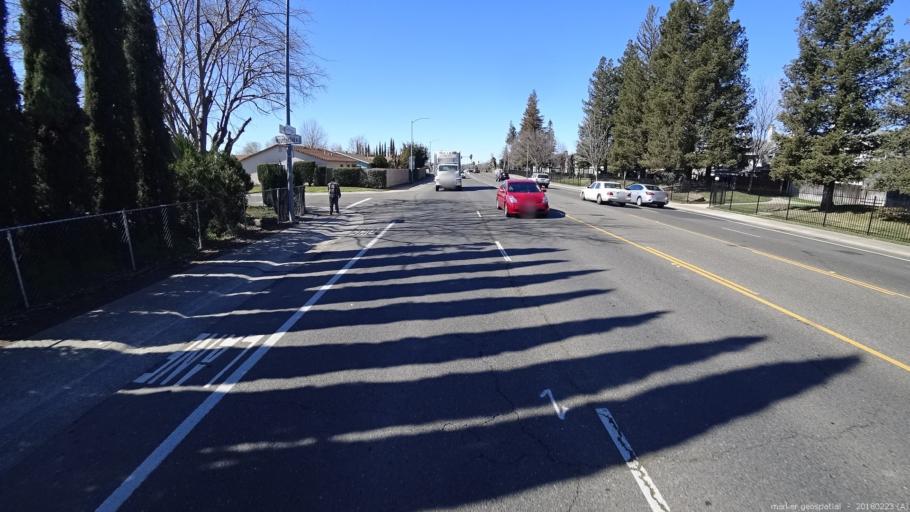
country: US
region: California
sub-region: Sacramento County
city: North Highlands
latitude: 38.7040
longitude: -121.3806
